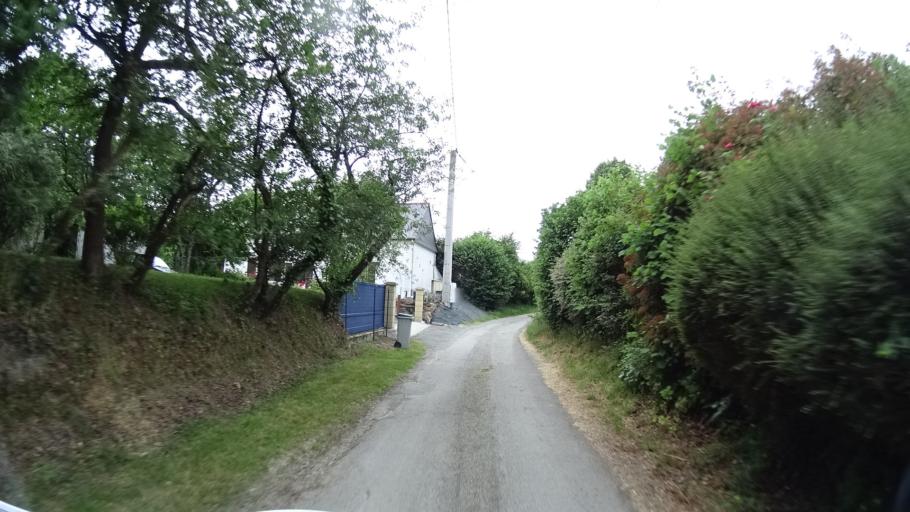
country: FR
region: Brittany
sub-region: Departement d'Ille-et-Vilaine
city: Crevin
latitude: 47.9619
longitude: -1.6789
